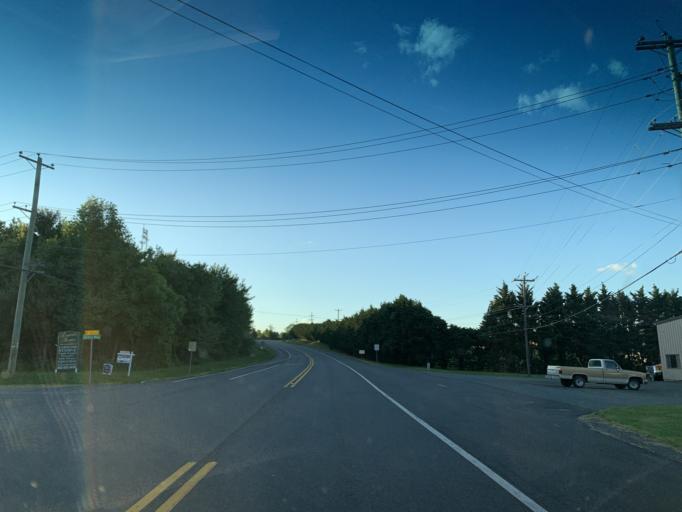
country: US
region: Maryland
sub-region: Cecil County
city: Elkton
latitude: 39.6759
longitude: -75.8591
